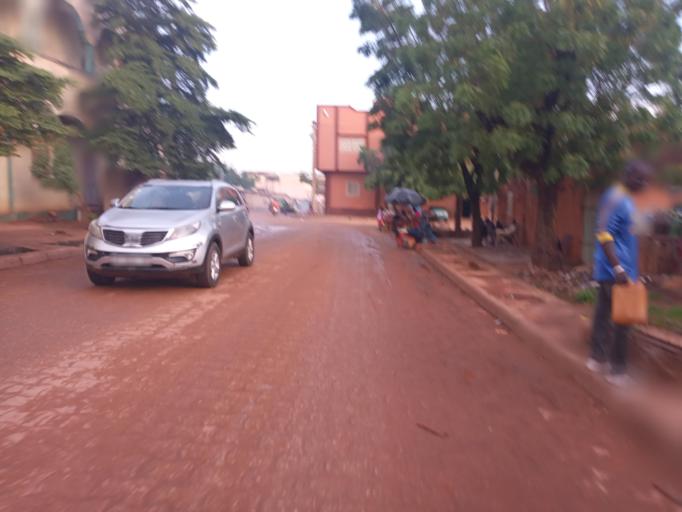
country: ML
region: Bamako
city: Bamako
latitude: 12.6418
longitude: -8.0308
